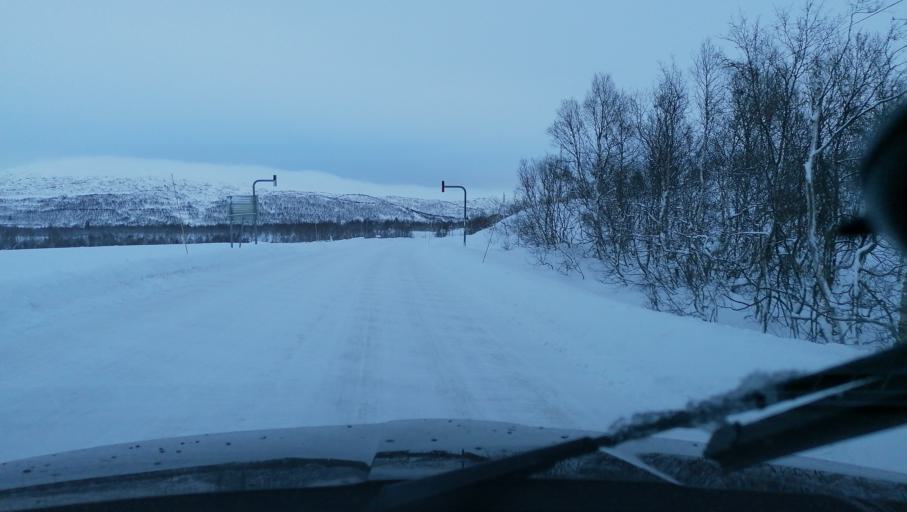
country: NO
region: Aust-Agder
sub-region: Bykle
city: Hovden
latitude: 59.6432
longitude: 7.4587
